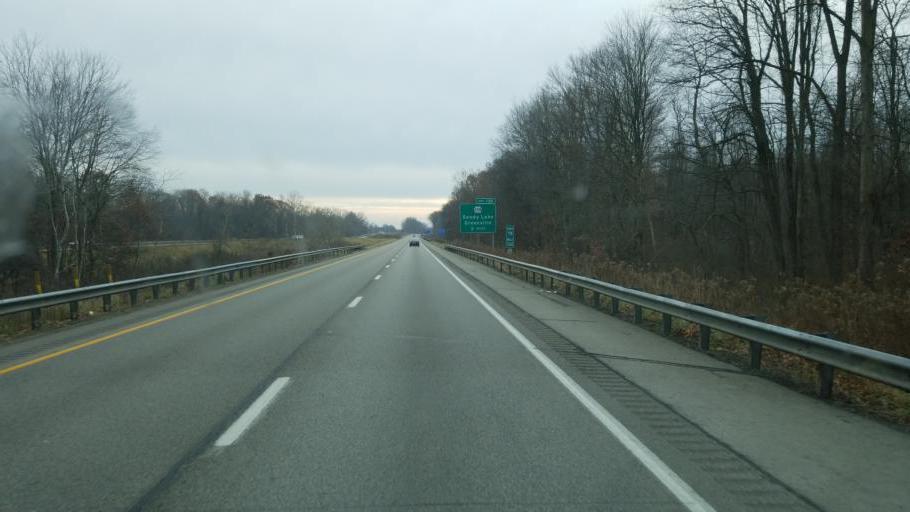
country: US
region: Pennsylvania
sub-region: Mercer County
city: Stoneboro
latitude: 41.4183
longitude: -80.1633
